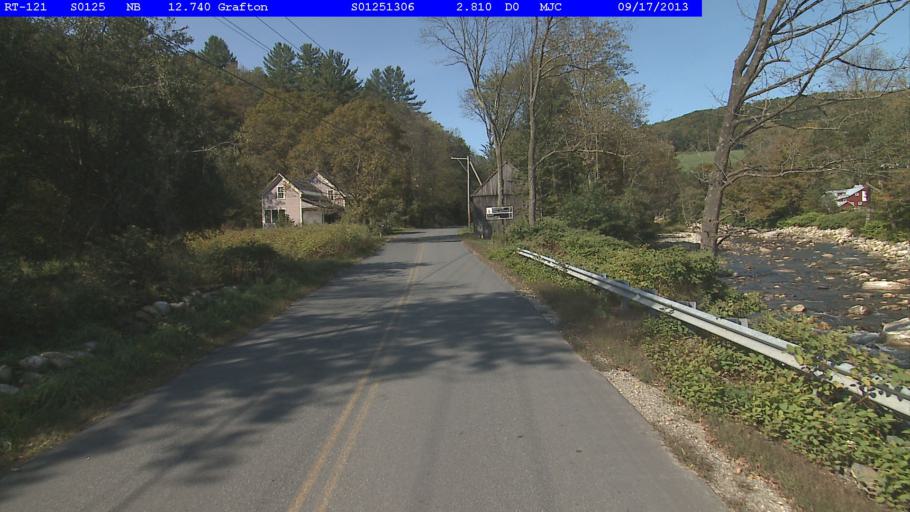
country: US
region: Vermont
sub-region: Windsor County
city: Chester
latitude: 43.1771
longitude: -72.5852
